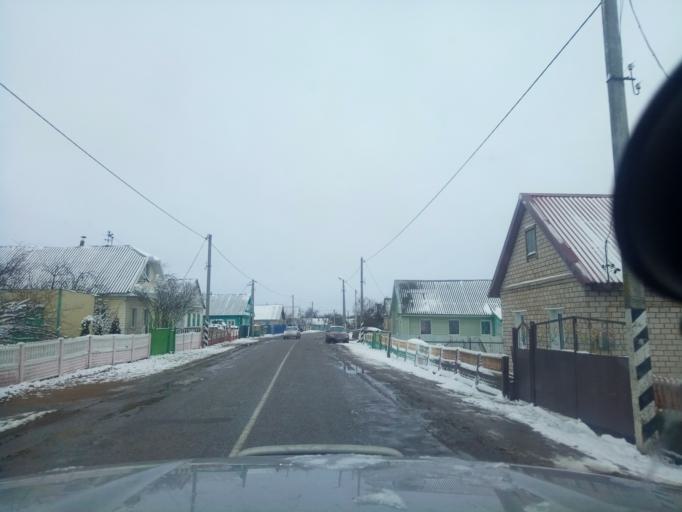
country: BY
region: Minsk
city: Tsimkavichy
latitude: 53.0738
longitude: 26.9964
